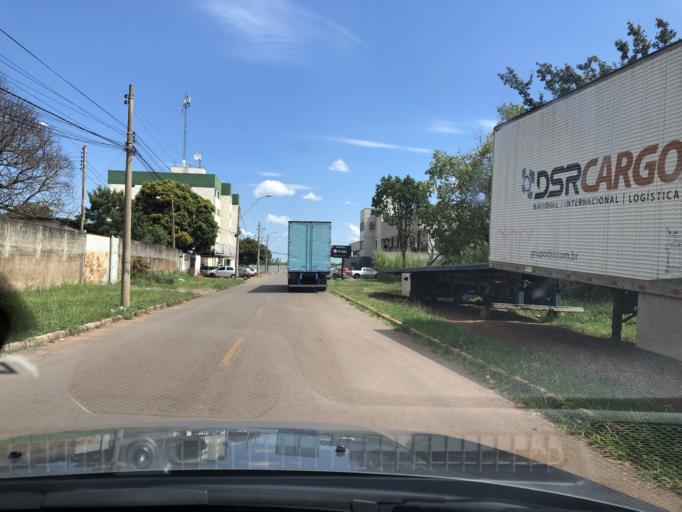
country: BR
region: Federal District
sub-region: Brasilia
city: Brasilia
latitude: -16.0054
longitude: -48.0549
